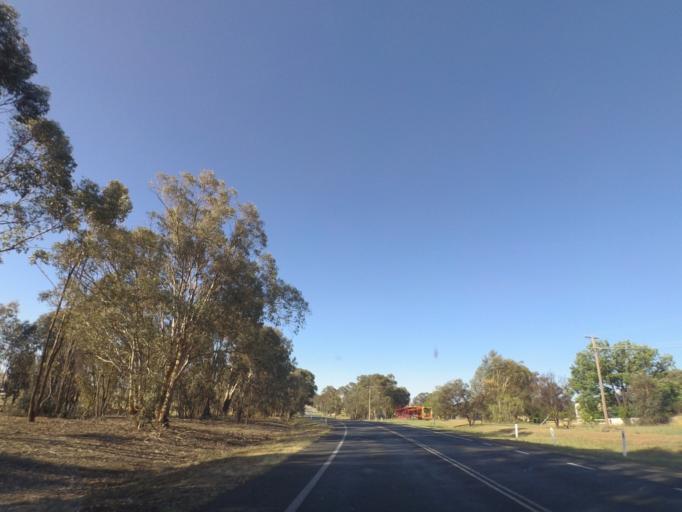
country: AU
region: New South Wales
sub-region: Wagga Wagga
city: Forest Hill
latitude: -35.2712
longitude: 147.7442
